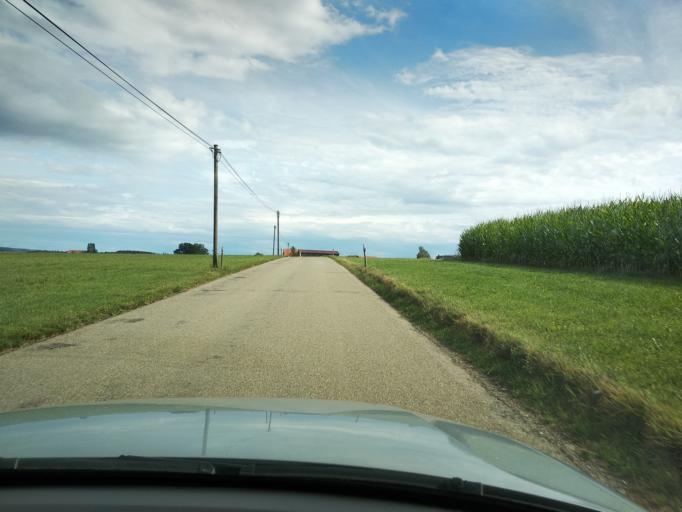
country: DE
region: Bavaria
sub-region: Swabia
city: Woringen
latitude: 47.8955
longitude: 10.1836
